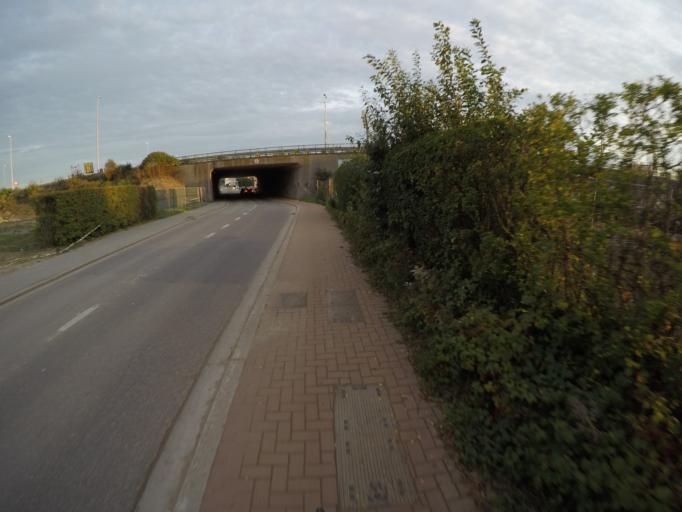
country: BE
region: Flanders
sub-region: Provincie Antwerpen
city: Zwijndrecht
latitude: 51.2117
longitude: 4.3433
